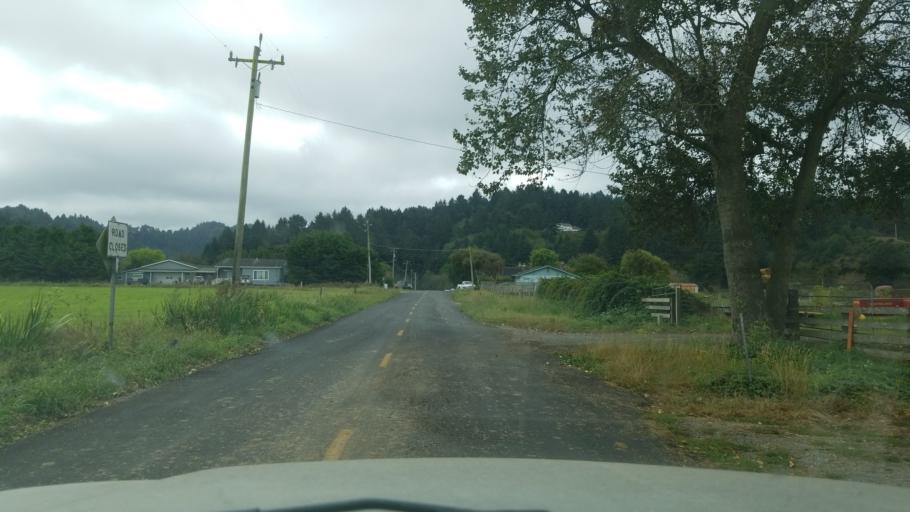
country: US
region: California
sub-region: Humboldt County
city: Ferndale
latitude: 40.5852
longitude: -124.2838
